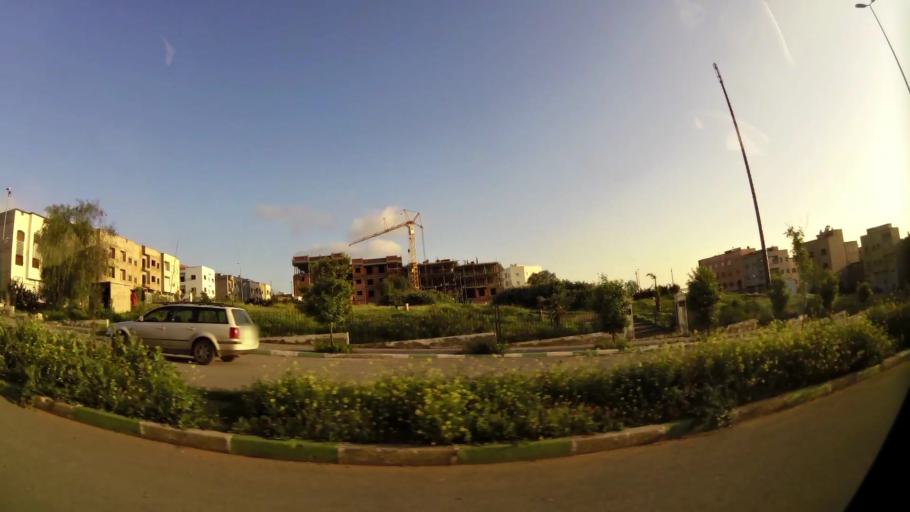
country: MA
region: Chaouia-Ouardigha
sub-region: Settat Province
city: Settat
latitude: 32.9880
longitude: -7.6049
